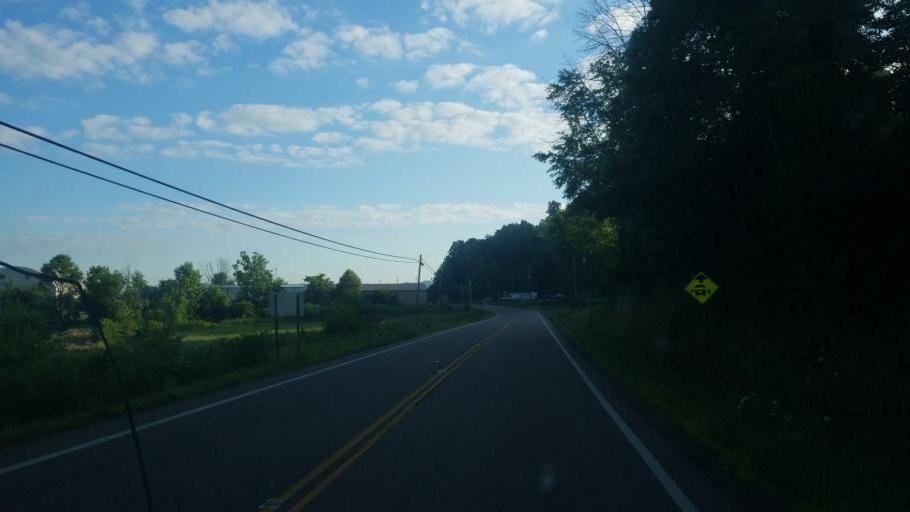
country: US
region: Ohio
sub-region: Holmes County
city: Millersburg
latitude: 40.5270
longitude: -81.9198
